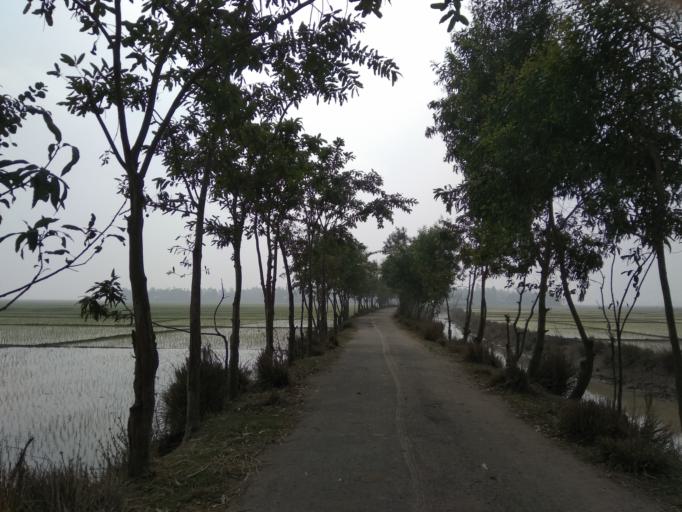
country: BD
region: Rajshahi
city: Bogra
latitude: 24.4715
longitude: 89.2686
